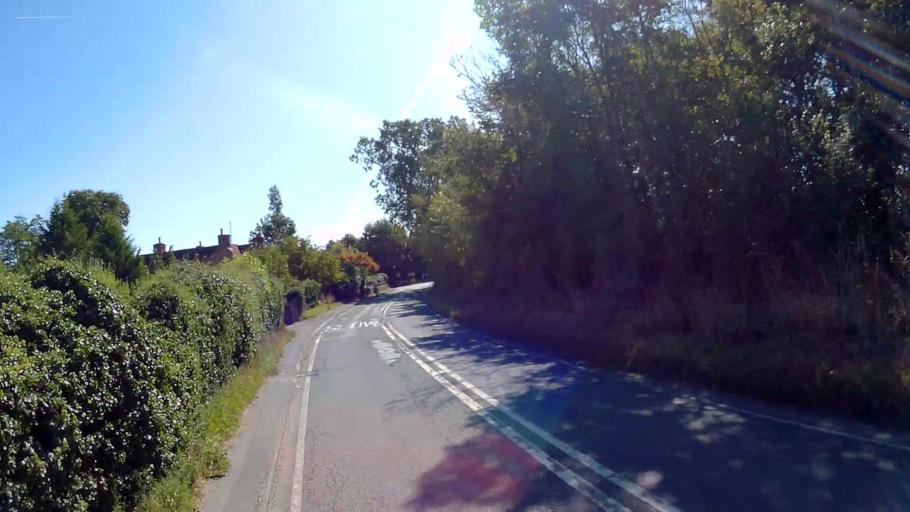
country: GB
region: England
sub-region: Wokingham
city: Swallowfield
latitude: 51.3812
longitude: -0.9644
